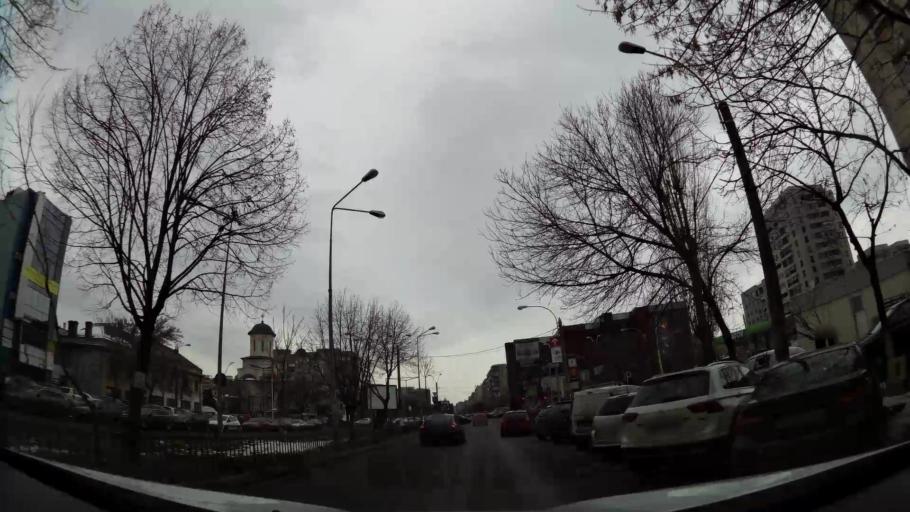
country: RO
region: Bucuresti
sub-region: Municipiul Bucuresti
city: Bucuresti
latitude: 44.4213
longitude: 26.0652
